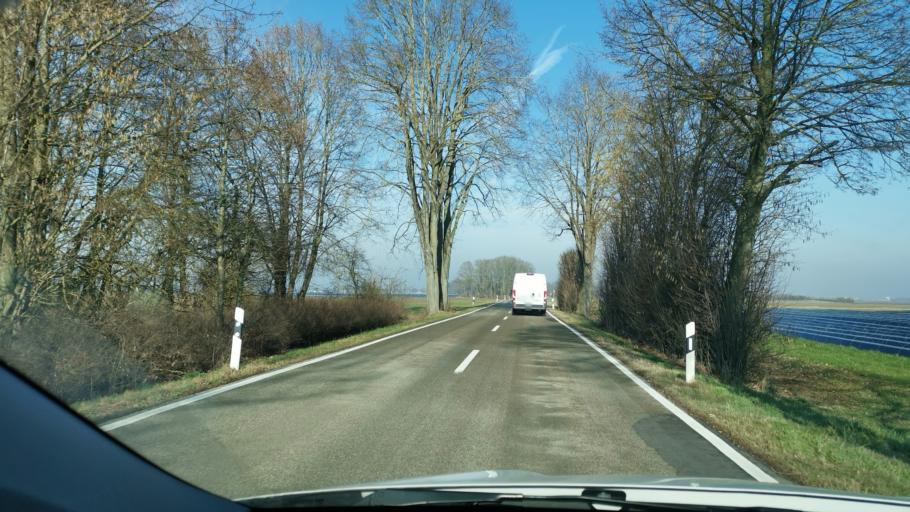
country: DE
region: Bavaria
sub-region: Swabia
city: Munster
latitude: 48.6314
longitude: 10.9269
